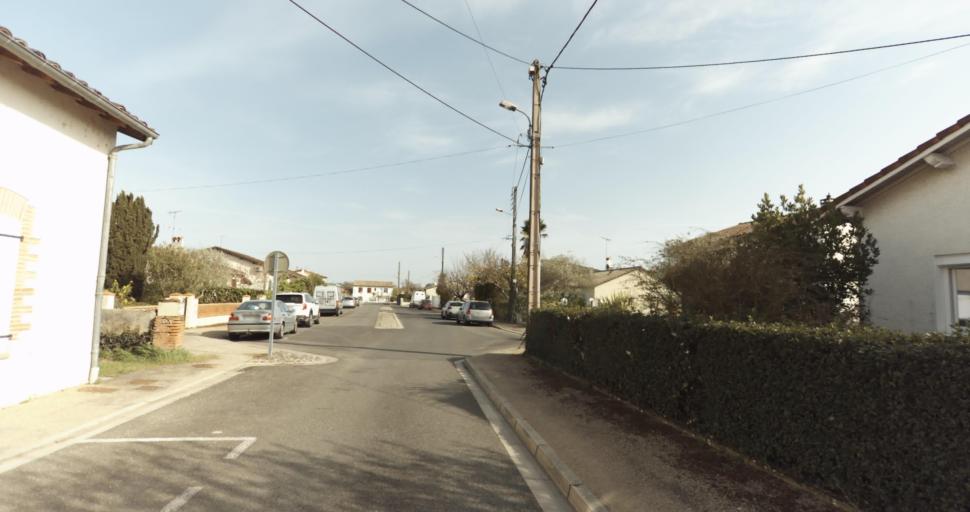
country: FR
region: Midi-Pyrenees
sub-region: Departement du Tarn
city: Saint-Sulpice-la-Pointe
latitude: 43.7733
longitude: 1.6913
